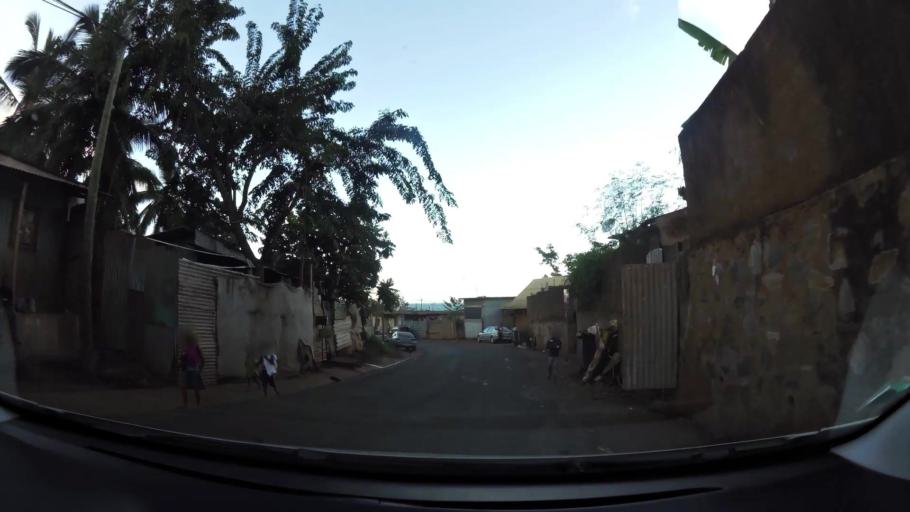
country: YT
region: Koungou
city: Koungou
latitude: -12.7367
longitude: 45.2045
